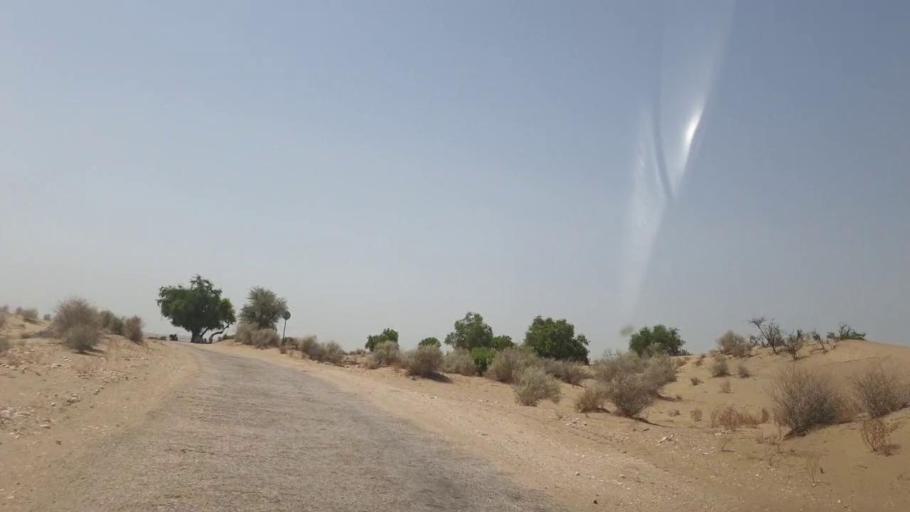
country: PK
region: Sindh
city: Khanpur
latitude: 27.3610
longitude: 69.3146
